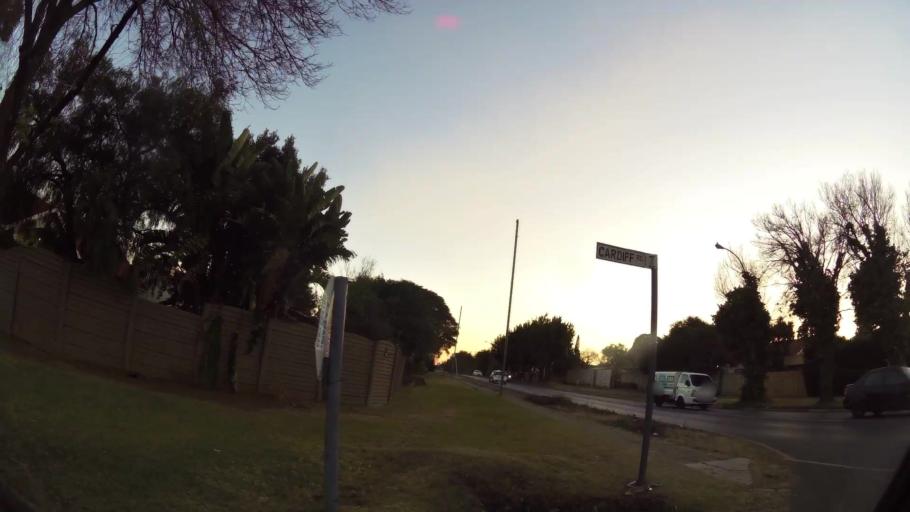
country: ZA
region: Gauteng
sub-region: Ekurhuleni Metropolitan Municipality
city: Germiston
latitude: -26.2641
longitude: 28.1624
